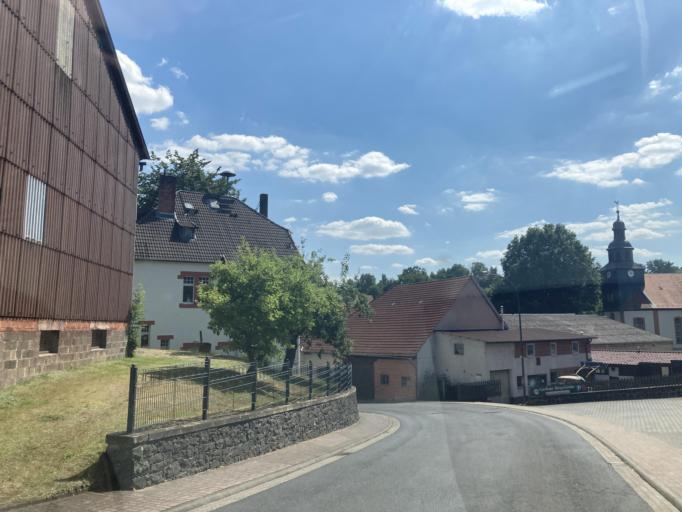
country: DE
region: Hesse
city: Grebenau
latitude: 50.7218
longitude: 9.4201
